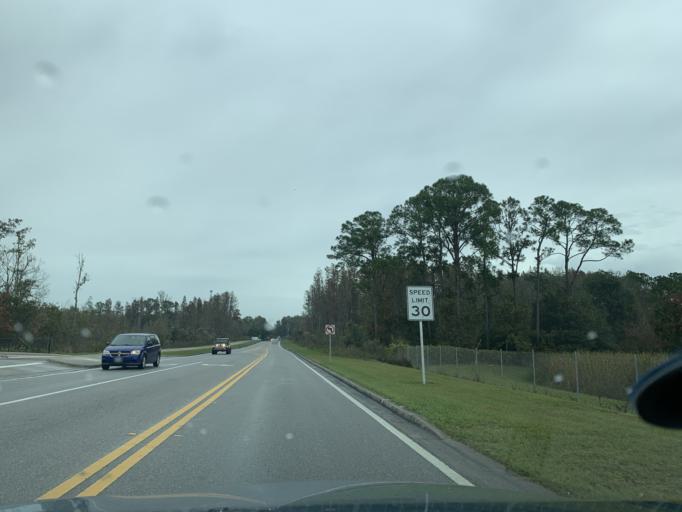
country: US
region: Florida
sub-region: Pasco County
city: Wesley Chapel
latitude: 28.2411
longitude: -82.3202
